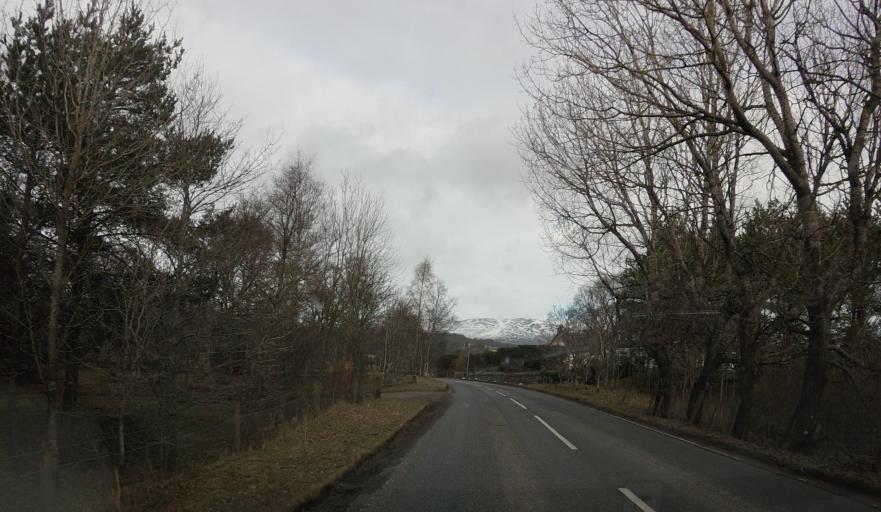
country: GB
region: Scotland
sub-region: Highland
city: Kingussie
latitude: 57.0537
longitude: -4.1305
